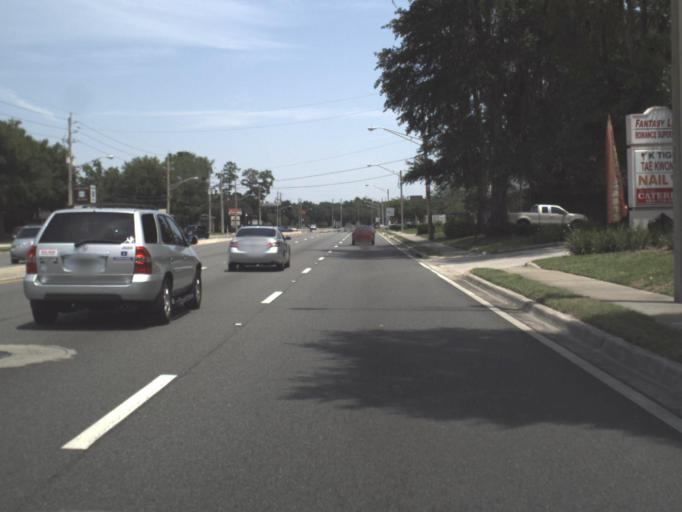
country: US
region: Florida
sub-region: Saint Johns County
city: Fruit Cove
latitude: 30.1616
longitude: -81.6325
